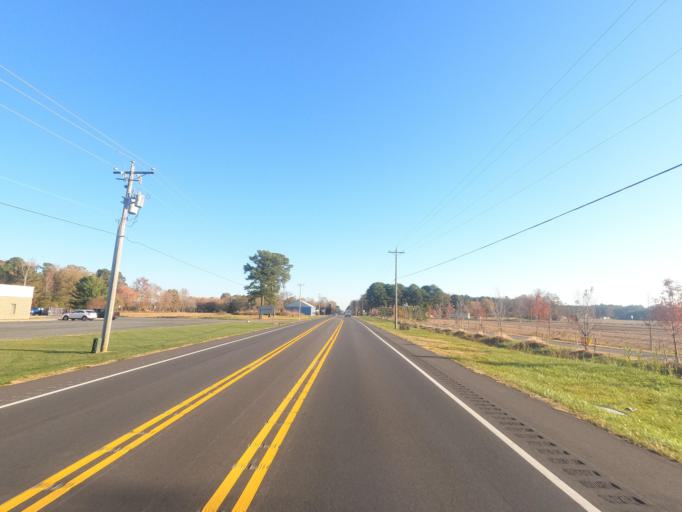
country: US
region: Maryland
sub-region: Somerset County
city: Crisfield
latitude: 38.0088
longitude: -75.8174
